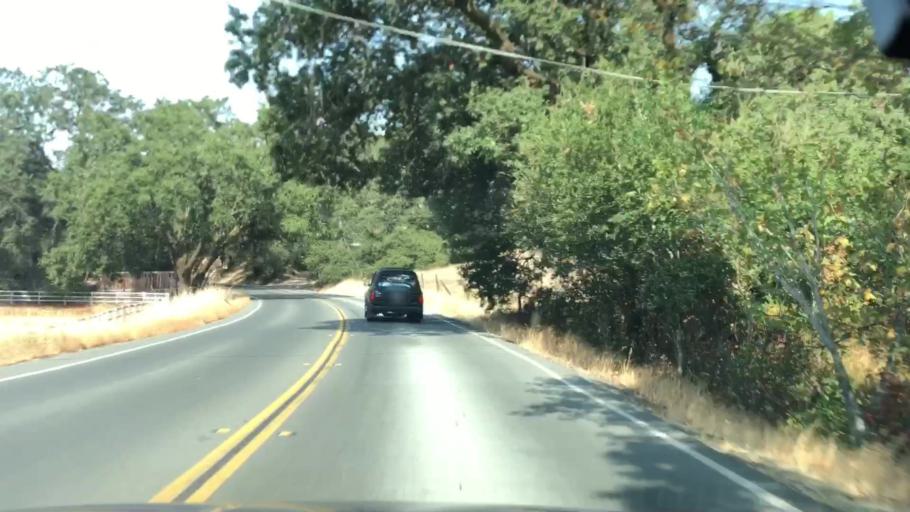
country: US
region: California
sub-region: Sonoma County
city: Larkfield-Wikiup
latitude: 38.5499
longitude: -122.7135
